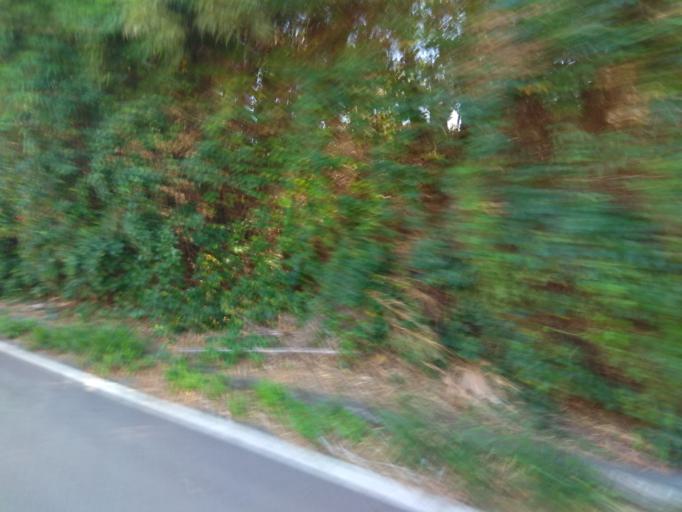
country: TW
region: Taiwan
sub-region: Hsinchu
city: Zhubei
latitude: 24.9460
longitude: 121.0001
